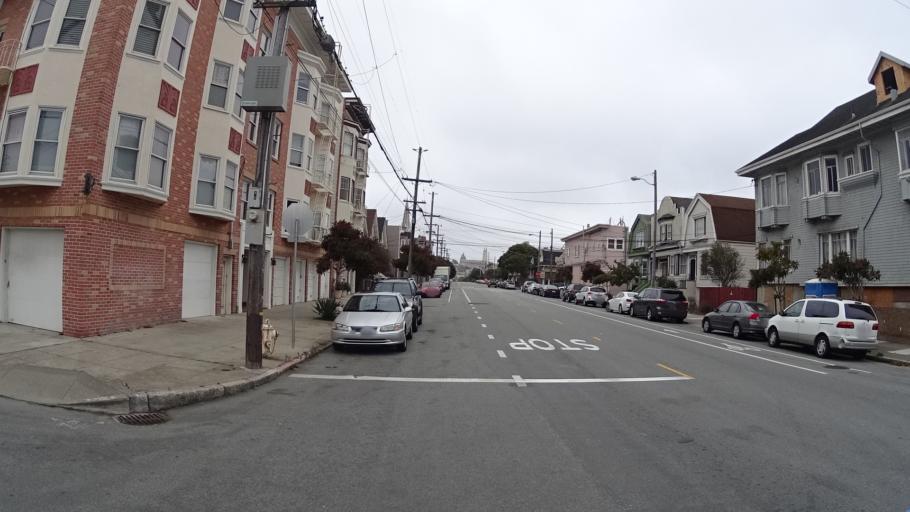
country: US
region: California
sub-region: San Francisco County
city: San Francisco
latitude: 37.7751
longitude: -122.4692
